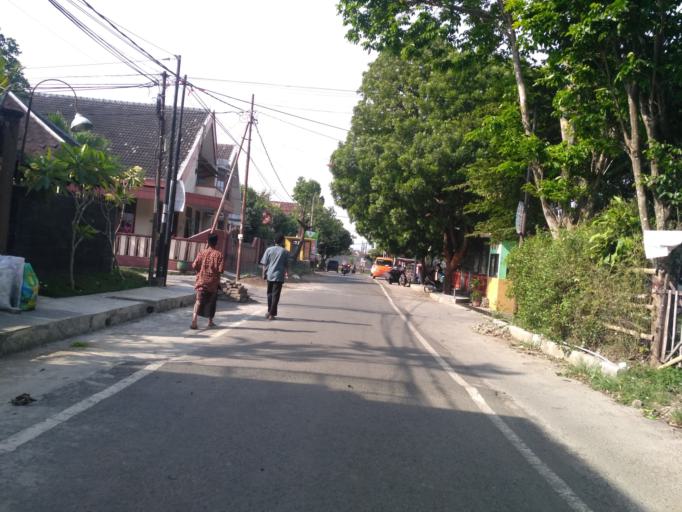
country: ID
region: East Java
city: Malang
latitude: -7.9388
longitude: 112.6089
